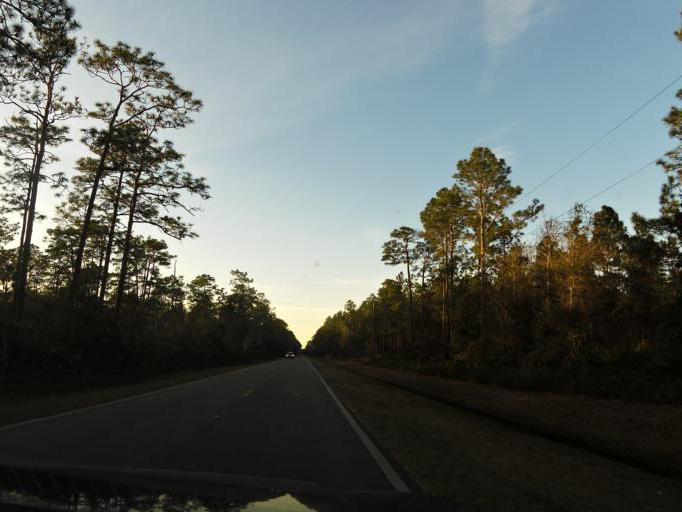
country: US
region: Florida
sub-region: Clay County
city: Green Cove Springs
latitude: 29.8785
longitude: -81.5548
